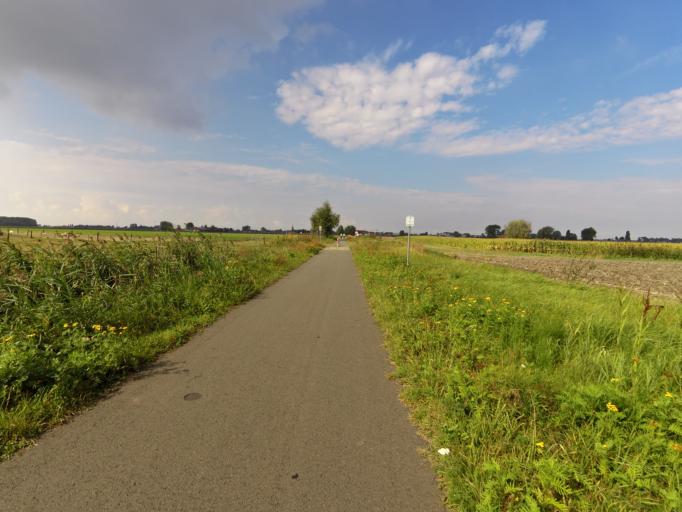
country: BE
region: Flanders
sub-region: Provincie West-Vlaanderen
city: Gistel
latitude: 51.1661
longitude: 2.9494
